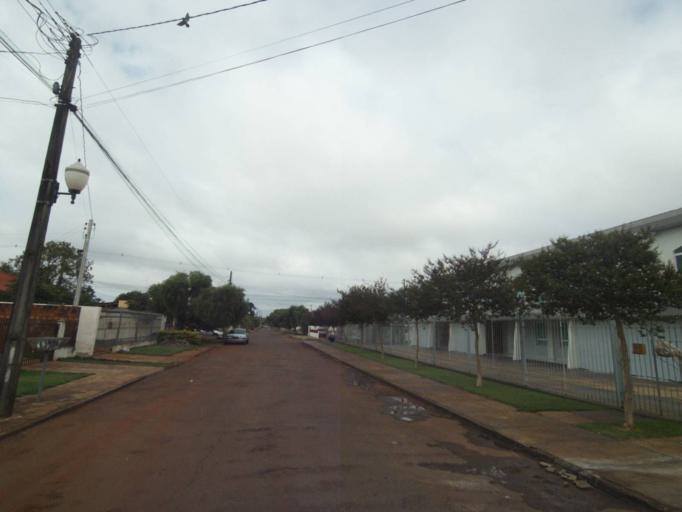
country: BR
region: Parana
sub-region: Campo Mourao
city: Campo Mourao
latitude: -24.0214
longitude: -52.3591
